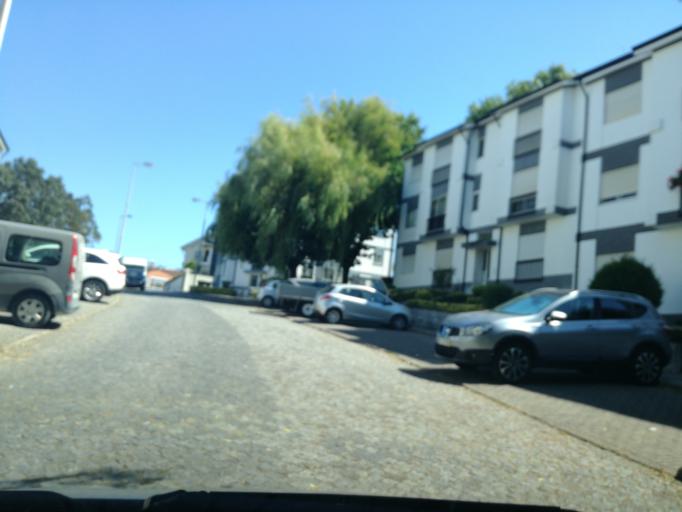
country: PT
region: Porto
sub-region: Maia
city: Maia
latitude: 41.2432
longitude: -8.6183
